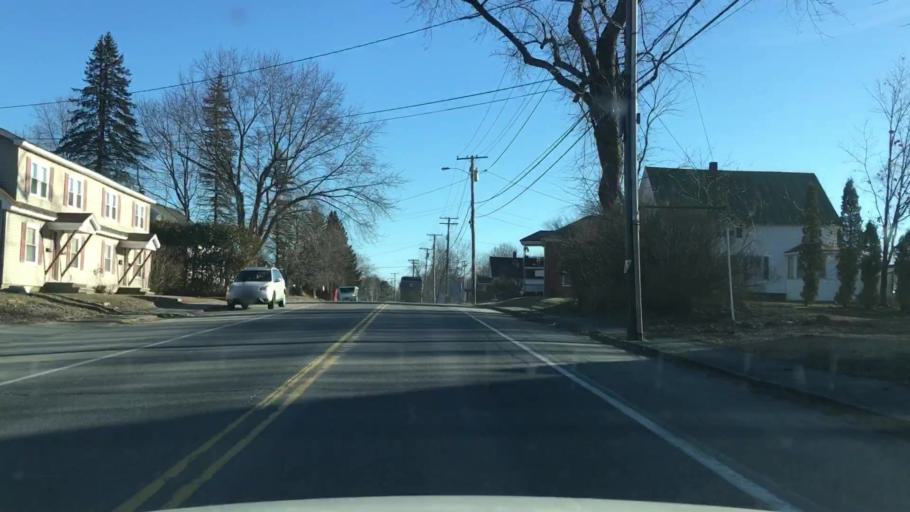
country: US
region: Maine
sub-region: Kennebec County
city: Winslow
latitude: 44.5418
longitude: -69.6185
